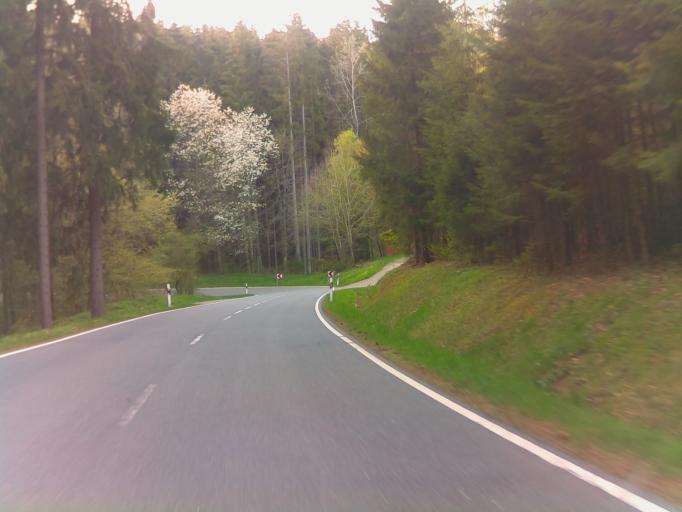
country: DE
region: Baden-Wuerttemberg
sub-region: Karlsruhe Region
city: Limbach
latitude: 49.4790
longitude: 9.1877
